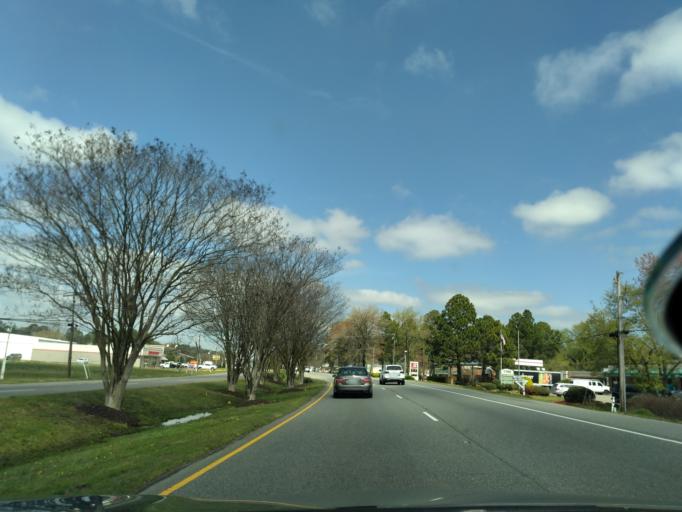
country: US
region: Virginia
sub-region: City of Poquoson
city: Poquoson
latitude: 37.1074
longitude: -76.4560
